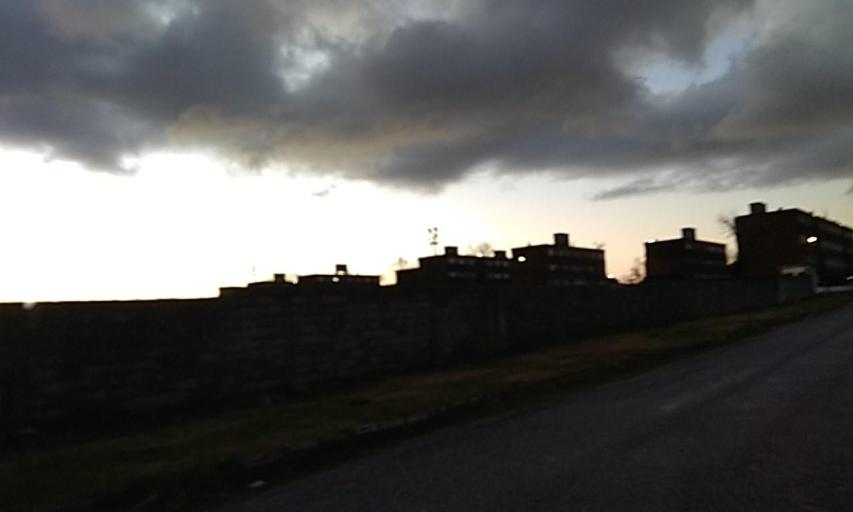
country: UY
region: Florida
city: Florida
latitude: -34.1094
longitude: -56.2132
